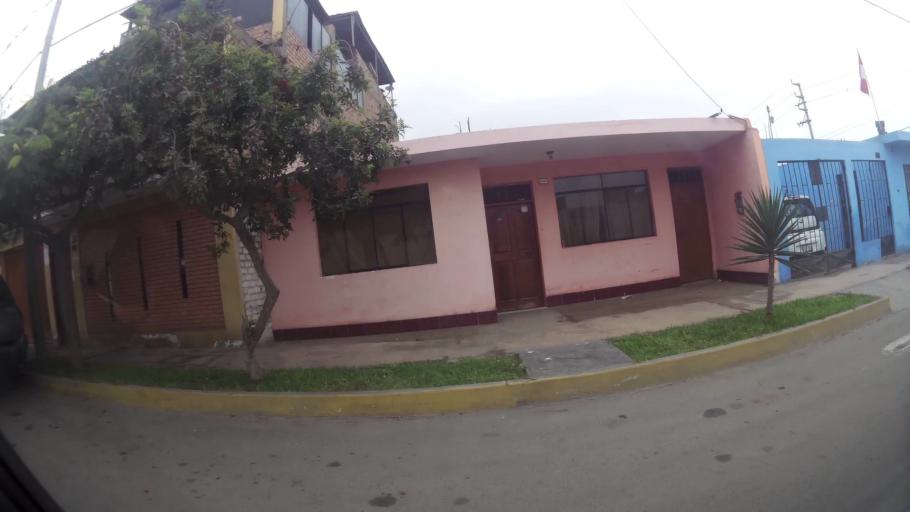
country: PE
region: Lima
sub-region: Provincia de Huaral
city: Chancay
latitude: -11.5695
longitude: -77.2707
